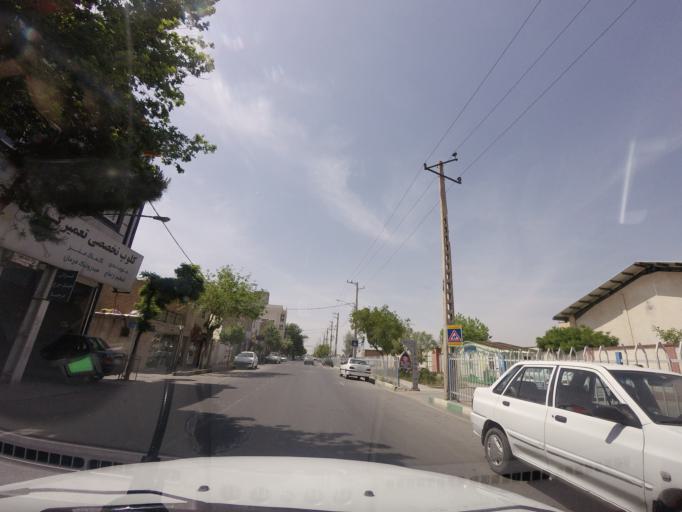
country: IR
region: Tehran
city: Eslamshahr
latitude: 35.6046
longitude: 51.2687
